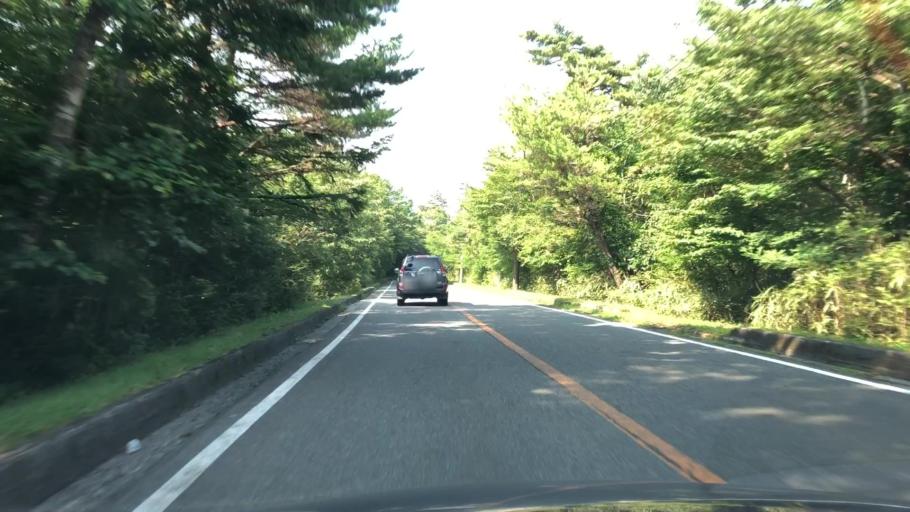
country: JP
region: Shizuoka
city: Gotemba
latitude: 35.3322
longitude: 138.8159
